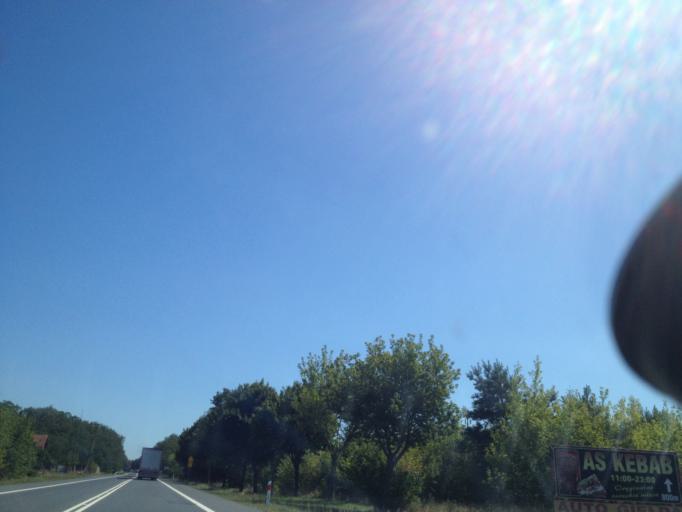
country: PL
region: Lubusz
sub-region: Powiat sulecinski
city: Torzym
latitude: 52.3161
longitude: 15.0478
